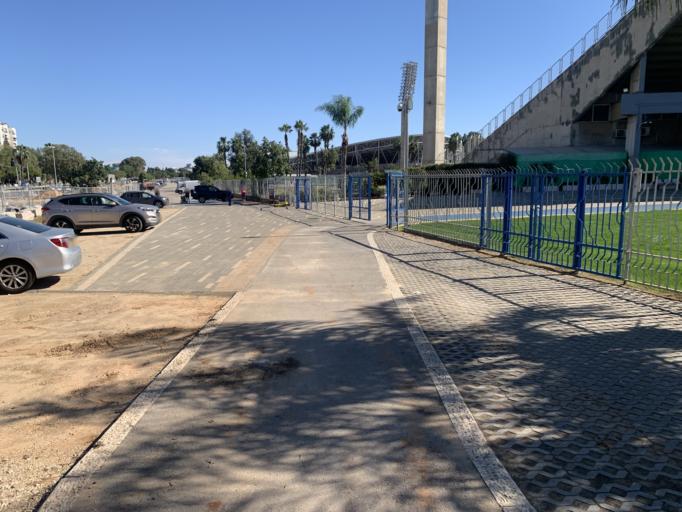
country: IL
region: Tel Aviv
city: Ramat Gan
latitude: 32.1057
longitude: 34.8214
